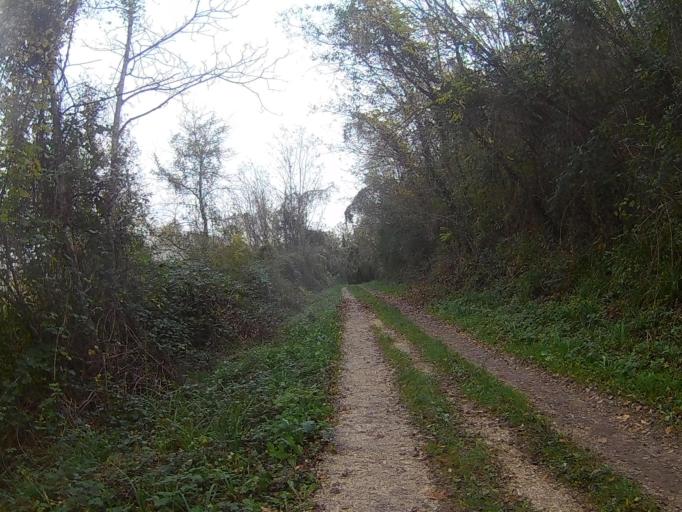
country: HR
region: Istarska
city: Karojba
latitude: 45.3438
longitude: 13.8356
